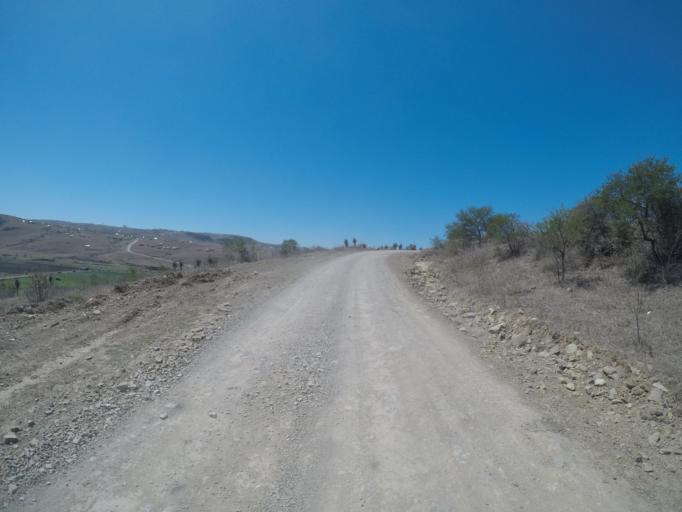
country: ZA
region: Eastern Cape
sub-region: OR Tambo District Municipality
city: Mthatha
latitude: -31.8729
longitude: 28.8703
